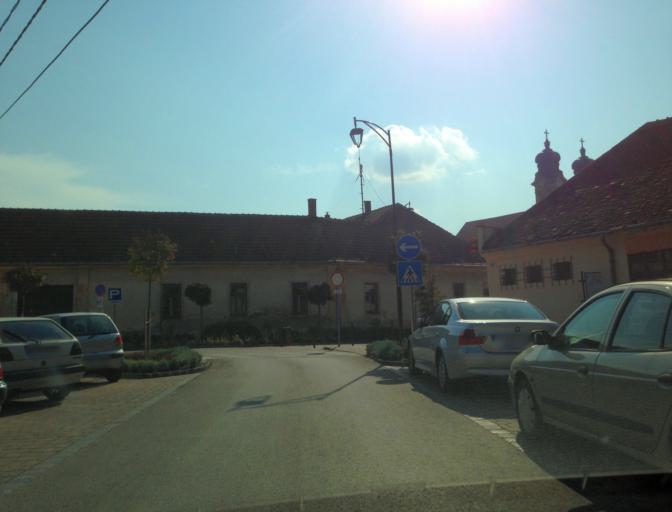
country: HU
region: Komarom-Esztergom
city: Tata
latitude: 47.6450
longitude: 18.3143
